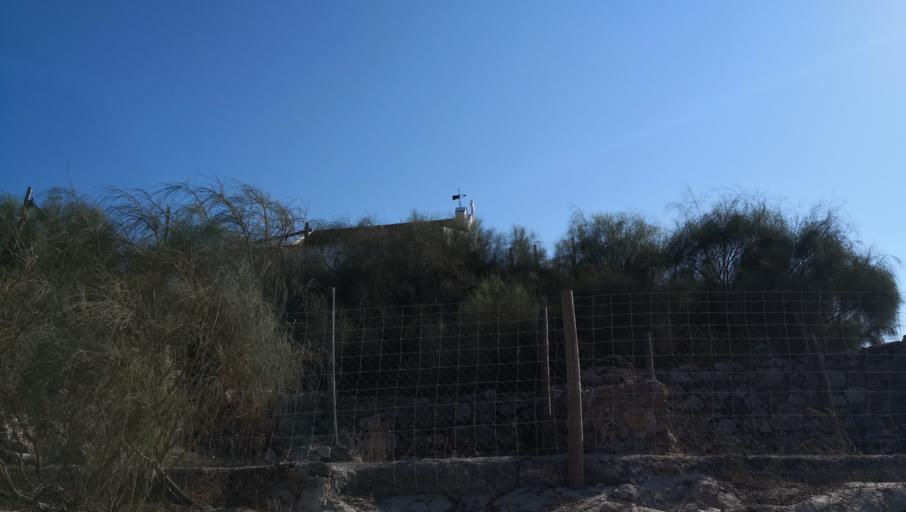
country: PT
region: Setubal
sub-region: Setubal
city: Setubal
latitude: 38.4871
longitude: -8.8858
